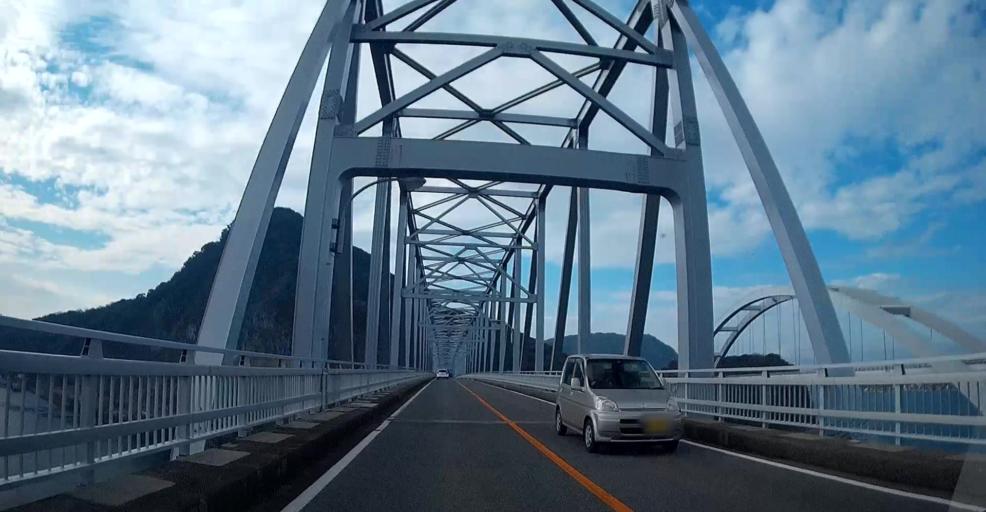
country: JP
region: Kumamoto
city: Yatsushiro
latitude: 32.6107
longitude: 130.4602
